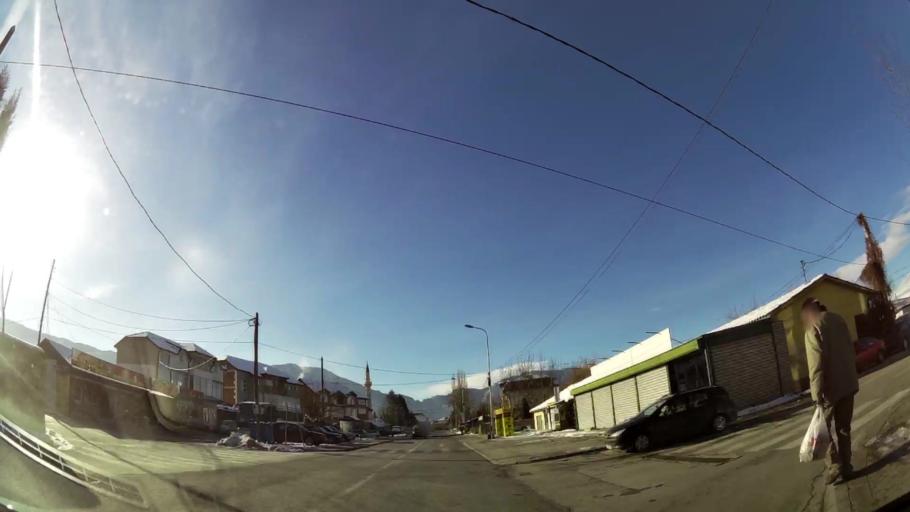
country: MK
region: Saraj
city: Saraj
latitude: 42.0033
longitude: 21.3317
